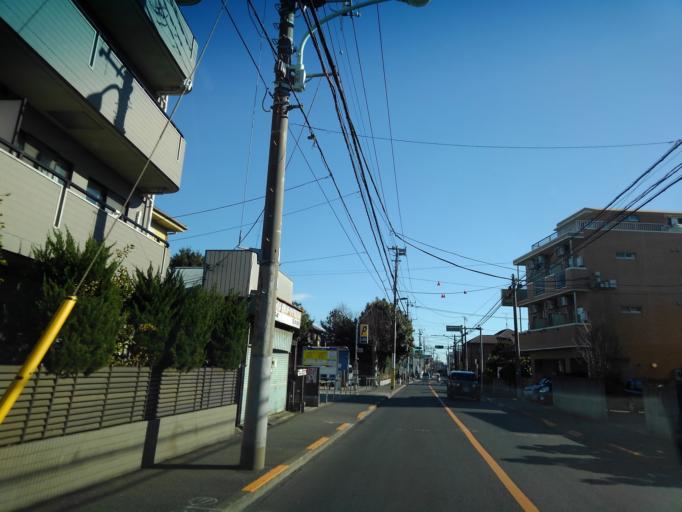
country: JP
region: Tokyo
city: Chofugaoka
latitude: 35.6636
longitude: 139.5201
